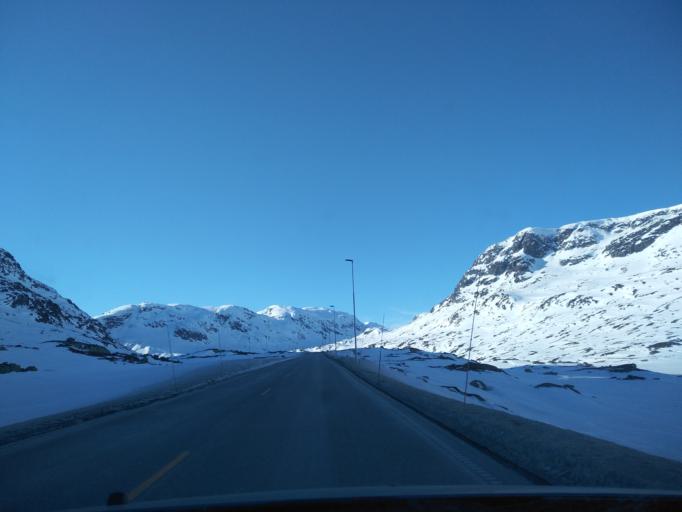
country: NO
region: Aust-Agder
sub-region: Bykle
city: Hovden
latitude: 59.8498
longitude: 7.1140
